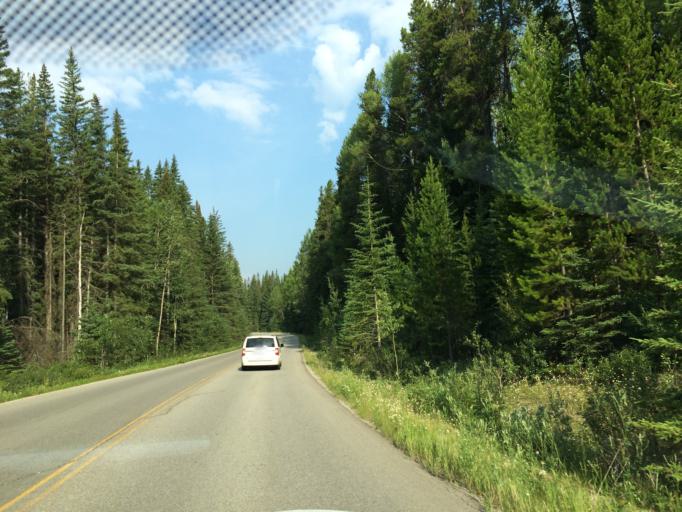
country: CA
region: Alberta
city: Banff
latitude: 51.1723
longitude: -115.7077
